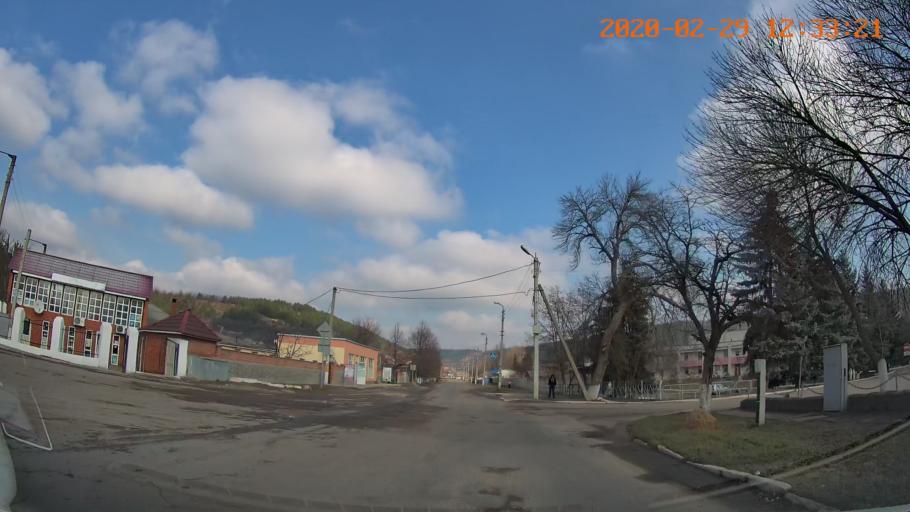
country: MD
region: Telenesti
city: Camenca
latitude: 48.0348
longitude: 28.7036
